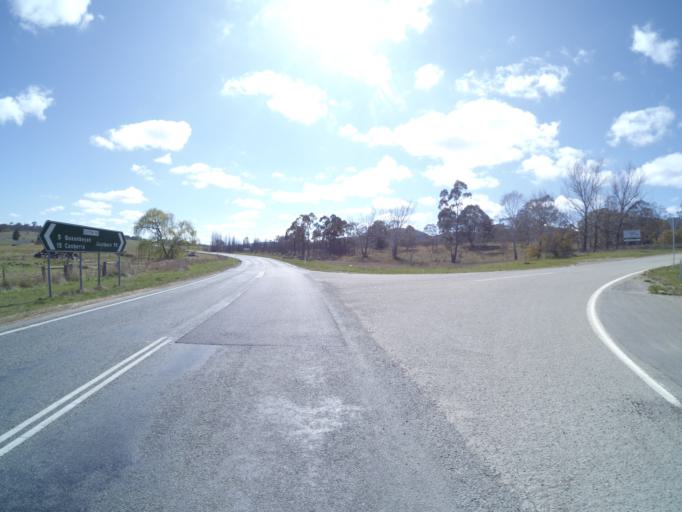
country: AU
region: New South Wales
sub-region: Queanbeyan
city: Queanbeyan
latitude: -35.3198
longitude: 149.2434
